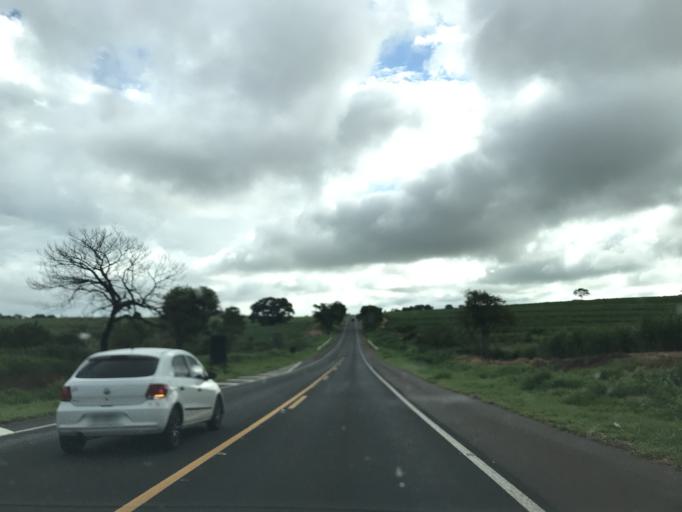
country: BR
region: Sao Paulo
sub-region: Penapolis
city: Penapolis
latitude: -21.4933
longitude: -50.2350
